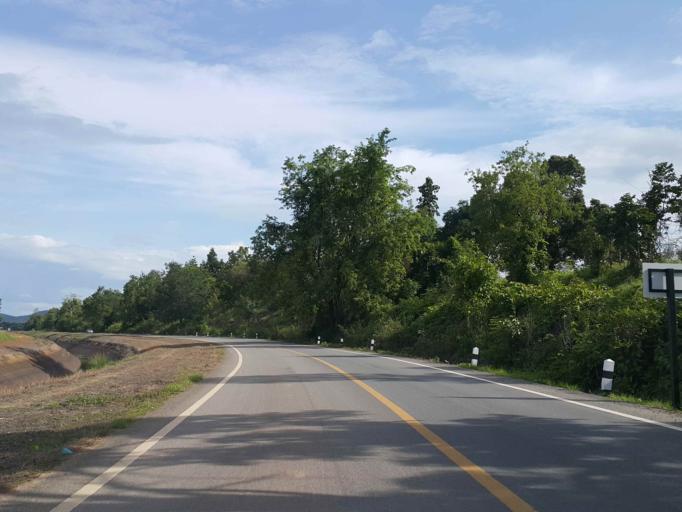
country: TH
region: Chiang Mai
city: San Sai
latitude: 18.8982
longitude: 99.1485
